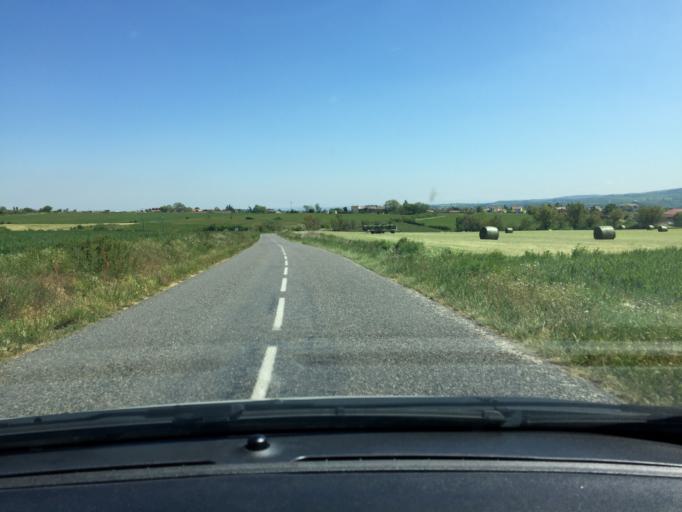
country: FR
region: Rhone-Alpes
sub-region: Departement du Rhone
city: Saint-Andeol-le-Chateau
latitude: 45.5880
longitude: 4.6788
